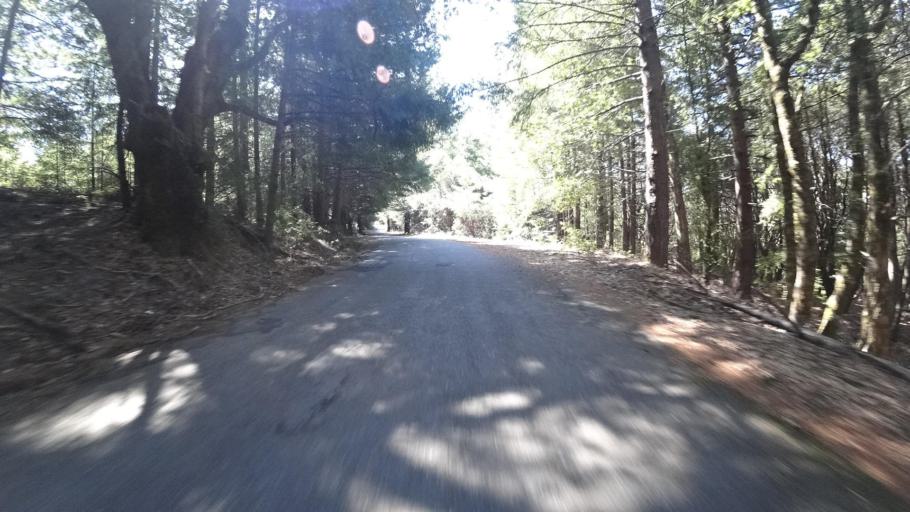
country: US
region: California
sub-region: Humboldt County
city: Redway
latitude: 40.1699
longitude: -124.0868
